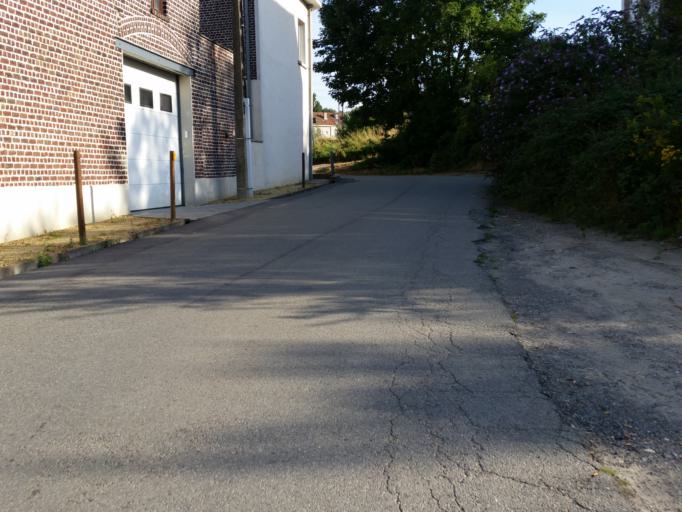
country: BE
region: Flanders
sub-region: Provincie Vlaams-Brabant
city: Diegem
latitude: 50.8956
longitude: 4.4314
